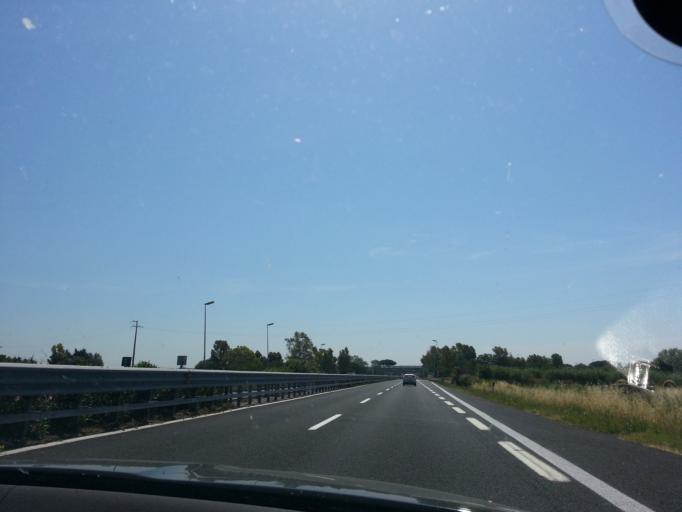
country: IT
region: Latium
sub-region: Citta metropolitana di Roma Capitale
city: Cerveteri
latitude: 41.9828
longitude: 12.0774
